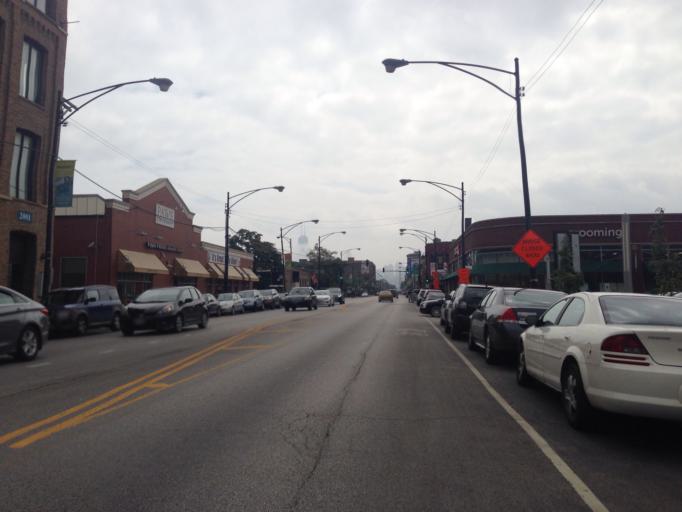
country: US
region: Illinois
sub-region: Cook County
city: Chicago
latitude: 41.9180
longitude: -87.6594
